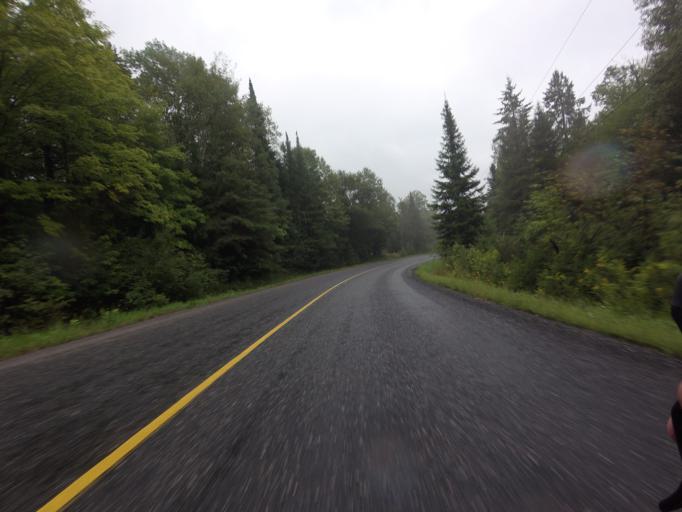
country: CA
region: Ontario
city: Perth
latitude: 45.0617
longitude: -76.5295
